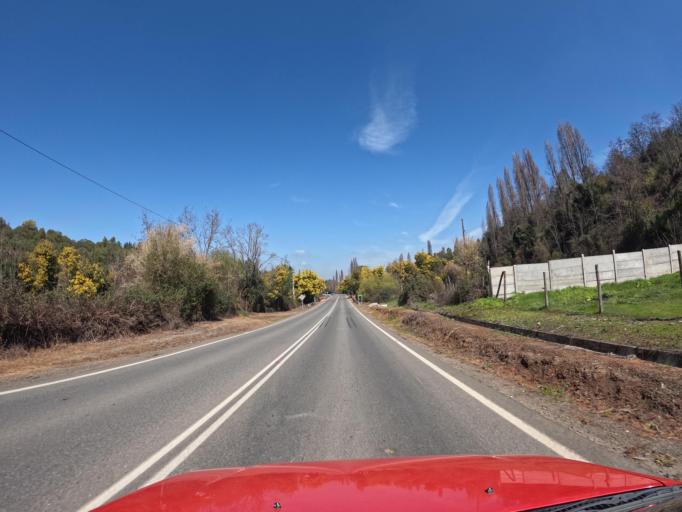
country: CL
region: Maule
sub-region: Provincia de Talca
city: San Clemente
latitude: -35.4565
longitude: -71.2691
